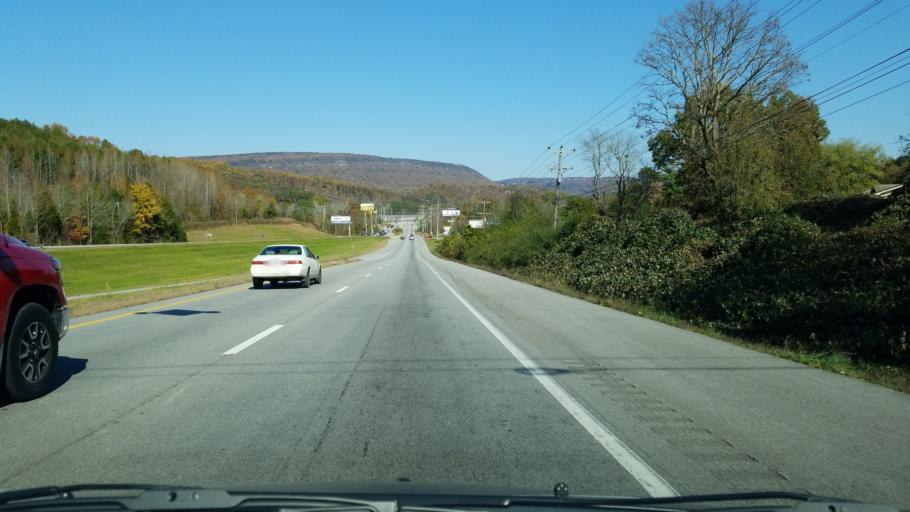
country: US
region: Tennessee
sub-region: Hamilton County
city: Falling Water
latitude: 35.1793
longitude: -85.2468
